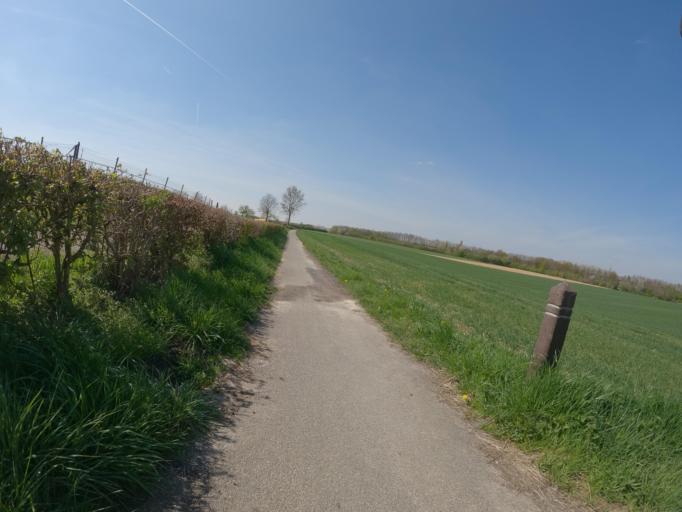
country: NL
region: Limburg
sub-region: Valkenburg aan de Geul
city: Sibbe
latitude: 50.8374
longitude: 5.8268
